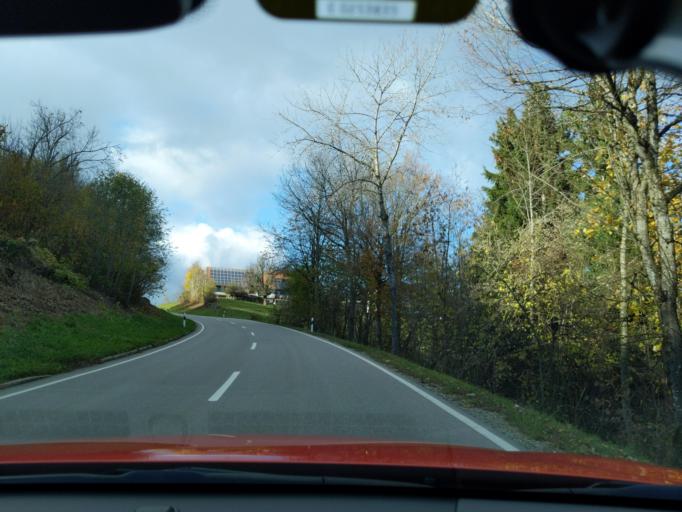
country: DE
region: Bavaria
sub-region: Swabia
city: Scheidegg
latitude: 47.5710
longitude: 9.8487
